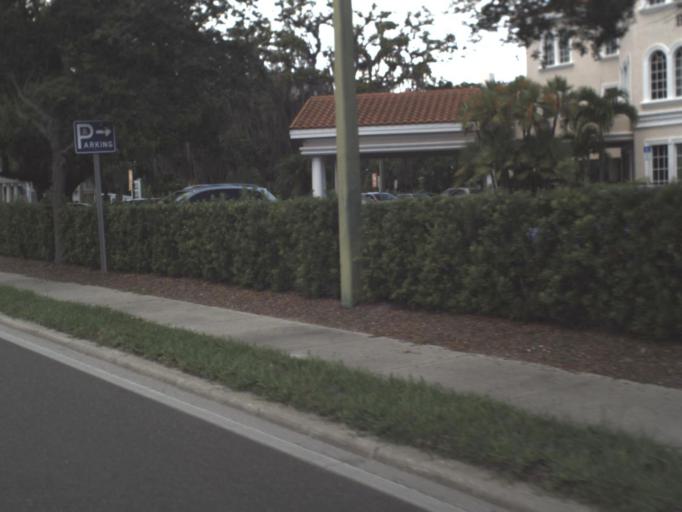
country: US
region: Florida
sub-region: Sarasota County
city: Sarasota
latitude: 27.3286
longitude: -82.5379
